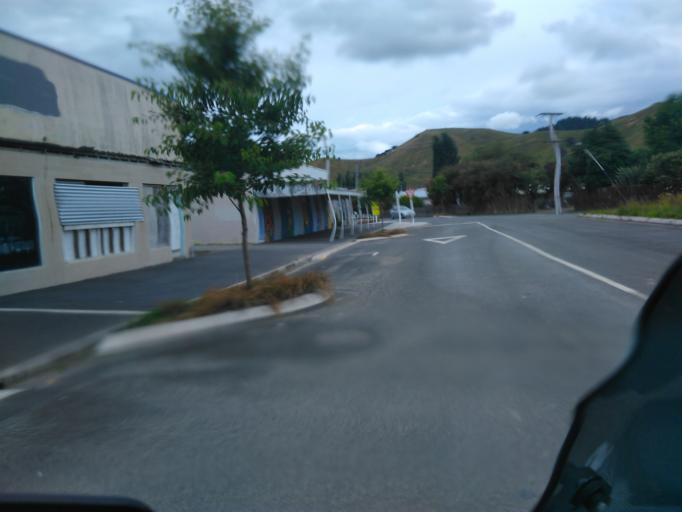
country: NZ
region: Gisborne
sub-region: Gisborne District
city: Gisborne
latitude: -38.4689
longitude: 177.8643
